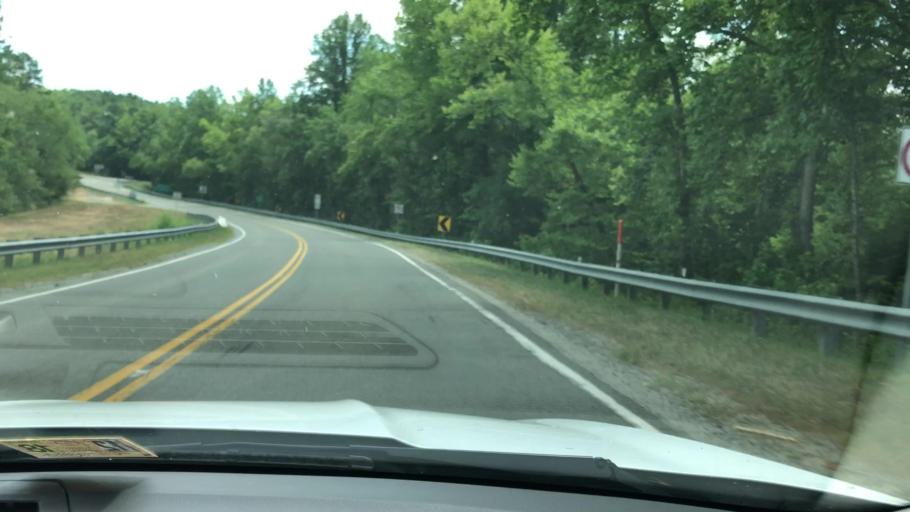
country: US
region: Virginia
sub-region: Lancaster County
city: Lancaster
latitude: 37.8317
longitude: -76.5776
